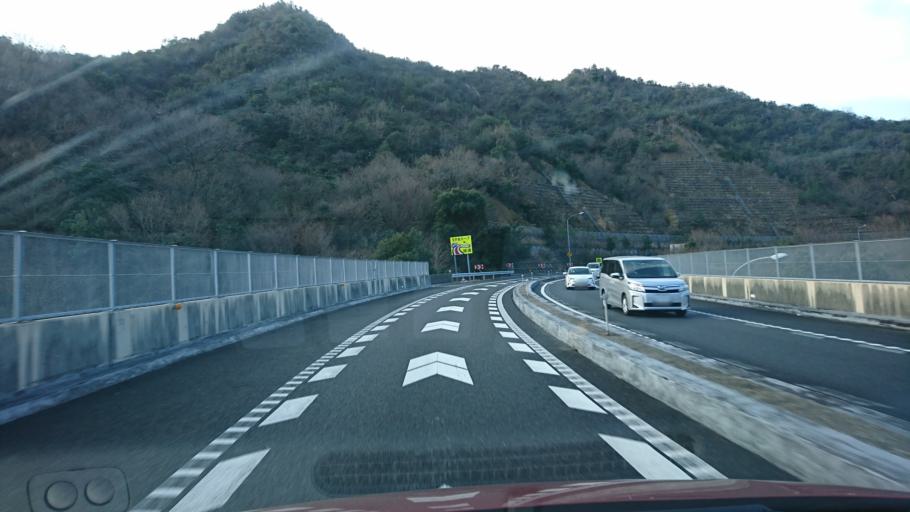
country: JP
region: Hyogo
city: Himeji
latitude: 34.8513
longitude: 134.7412
